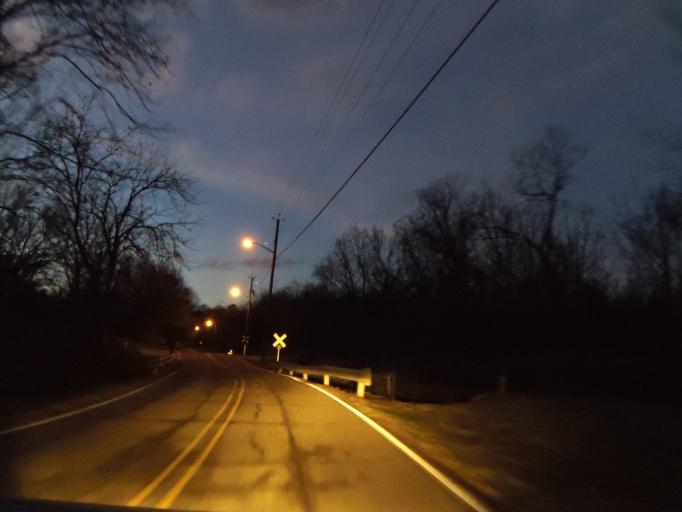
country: US
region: Tennessee
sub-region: Knox County
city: Knoxville
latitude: 35.9518
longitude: -83.8650
